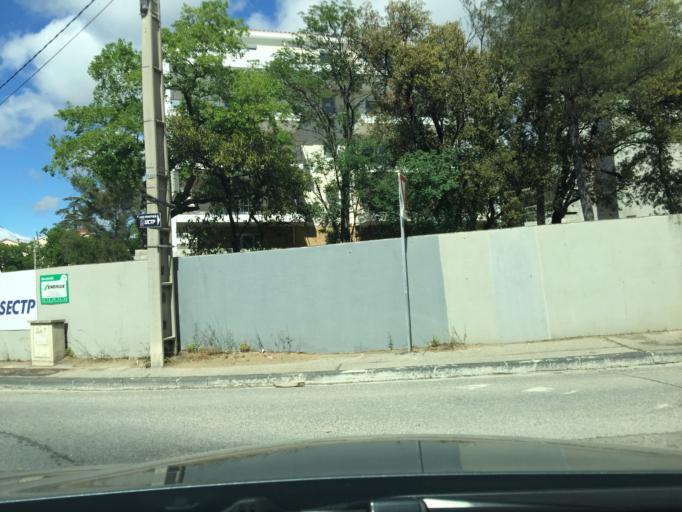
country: FR
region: Provence-Alpes-Cote d'Azur
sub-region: Departement des Bouches-du-Rhone
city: Marseille 10
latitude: 43.2665
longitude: 5.4269
